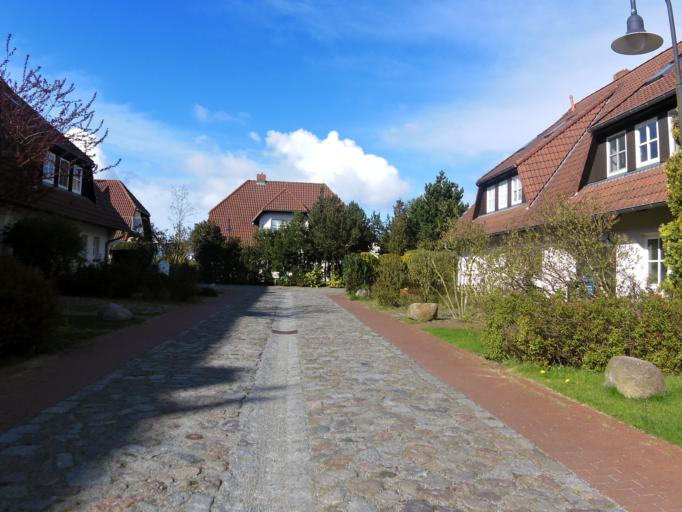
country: DE
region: Mecklenburg-Vorpommern
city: Zingst
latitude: 54.4375
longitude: 12.6944
